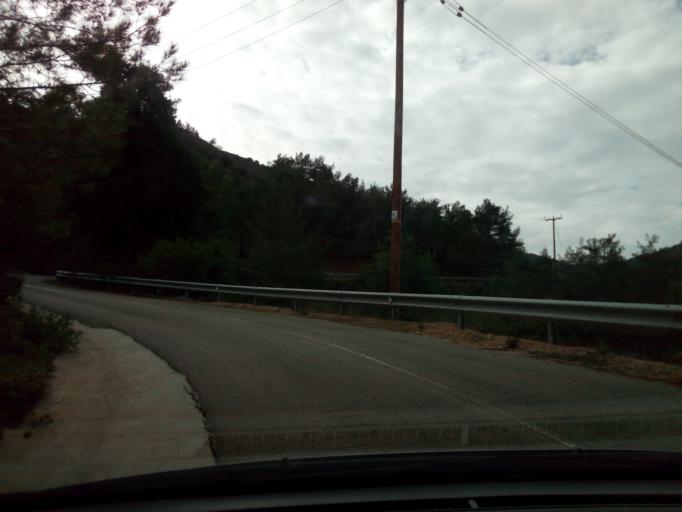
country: CY
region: Lefkosia
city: Klirou
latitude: 34.9717
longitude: 33.1786
